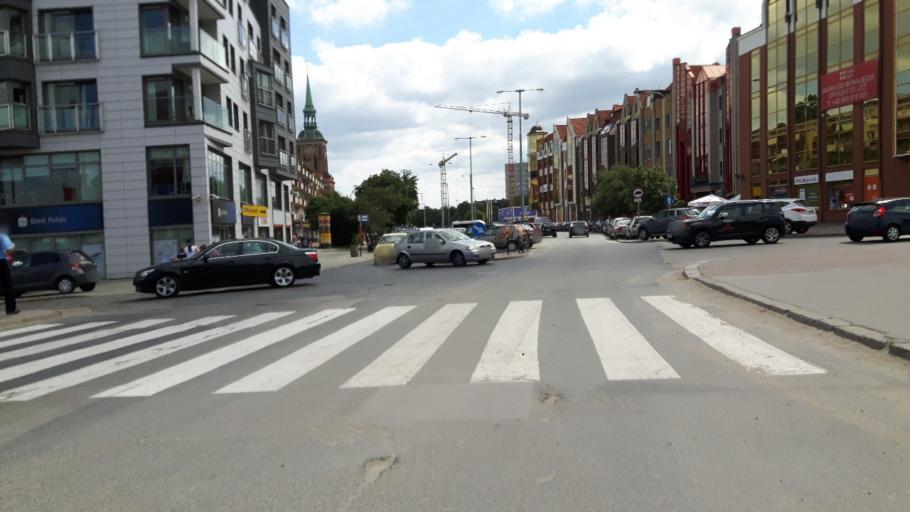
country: PL
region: Pomeranian Voivodeship
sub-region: Gdansk
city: Gdansk
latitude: 54.3474
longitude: 18.6603
